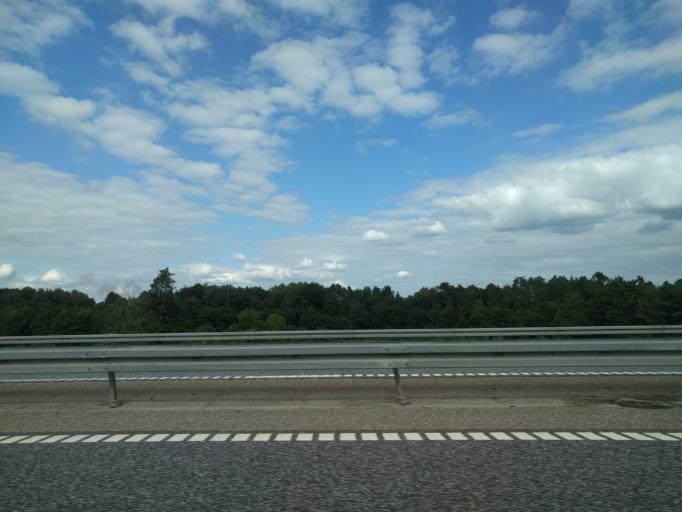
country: DK
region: Central Jutland
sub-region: Ikast-Brande Kommune
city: Brande
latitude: 55.9611
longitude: 9.1094
